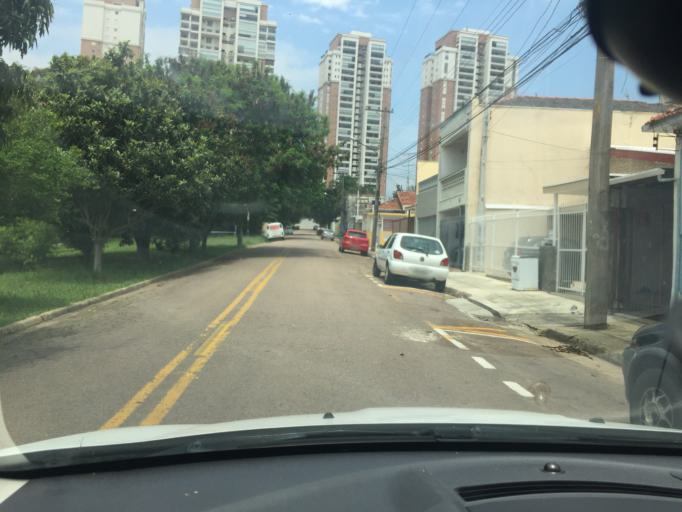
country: BR
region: Sao Paulo
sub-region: Jundiai
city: Jundiai
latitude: -23.1964
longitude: -46.8881
